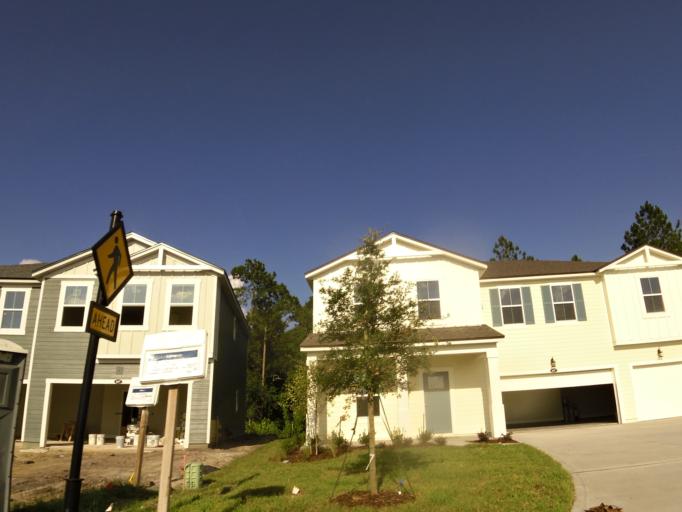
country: US
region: Florida
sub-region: Clay County
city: Green Cove Springs
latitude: 30.0290
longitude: -81.6299
